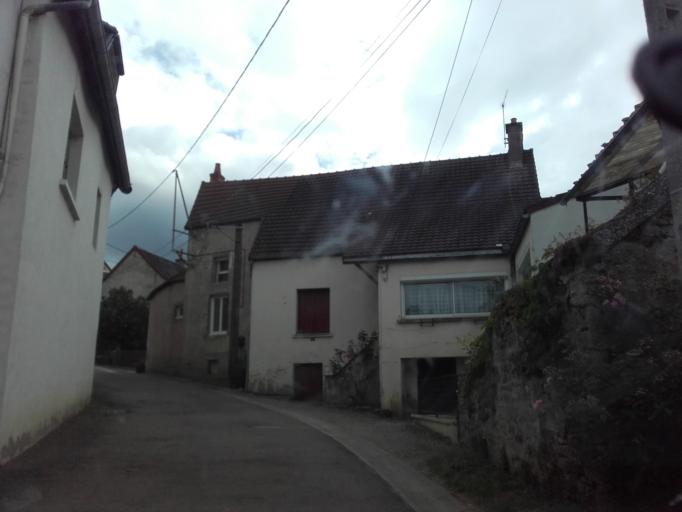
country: FR
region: Bourgogne
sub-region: Departement de Saone-et-Loire
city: Saint-Leger-sur-Dheune
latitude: 46.8746
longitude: 4.6660
